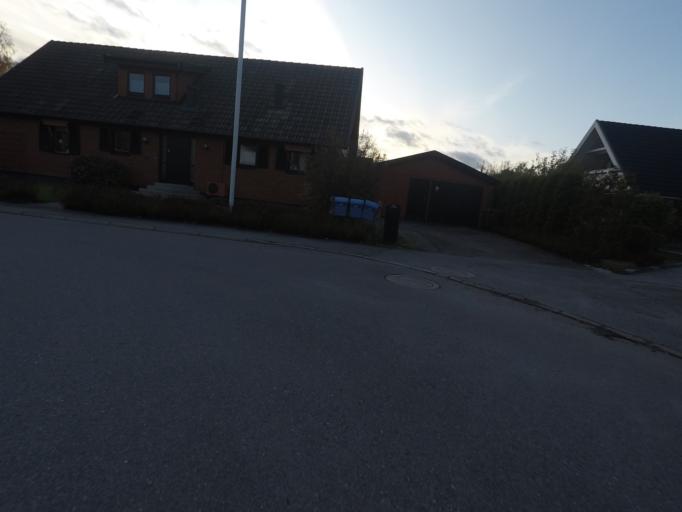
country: SE
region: OErebro
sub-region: Karlskoga Kommun
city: Karlskoga
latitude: 59.3107
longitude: 14.4761
